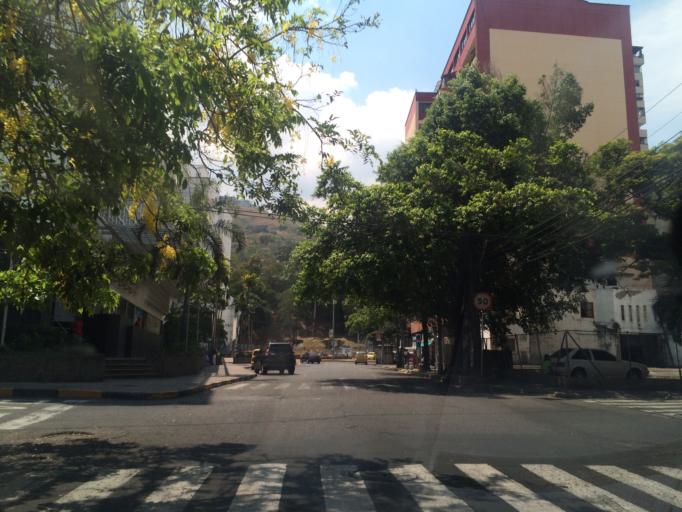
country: CO
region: Valle del Cauca
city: Cali
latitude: 3.4538
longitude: -76.5363
